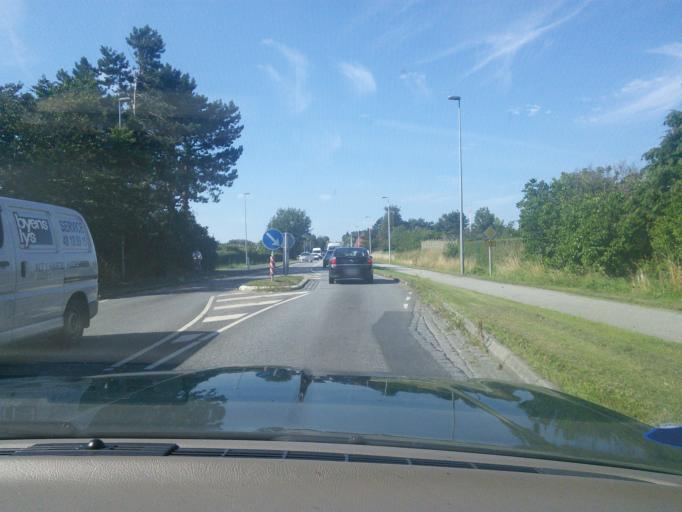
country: DK
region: Capital Region
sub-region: Halsnaes Kommune
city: Frederiksvaerk
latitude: 55.9495
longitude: 12.0447
